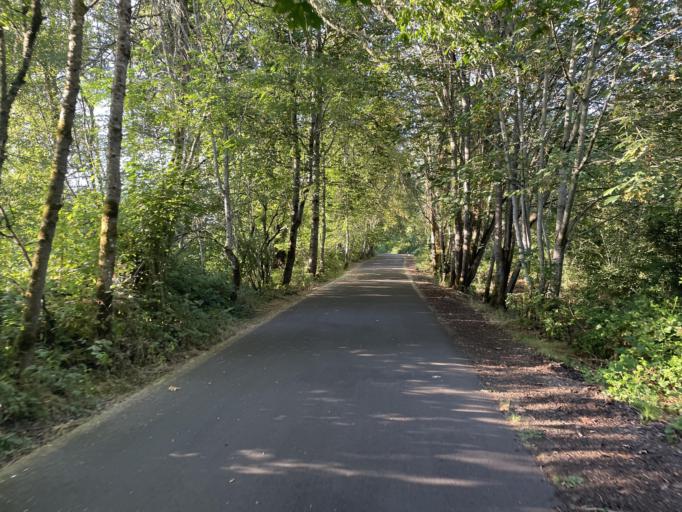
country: US
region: Oregon
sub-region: Marion County
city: Salem
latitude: 44.9198
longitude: -123.0754
